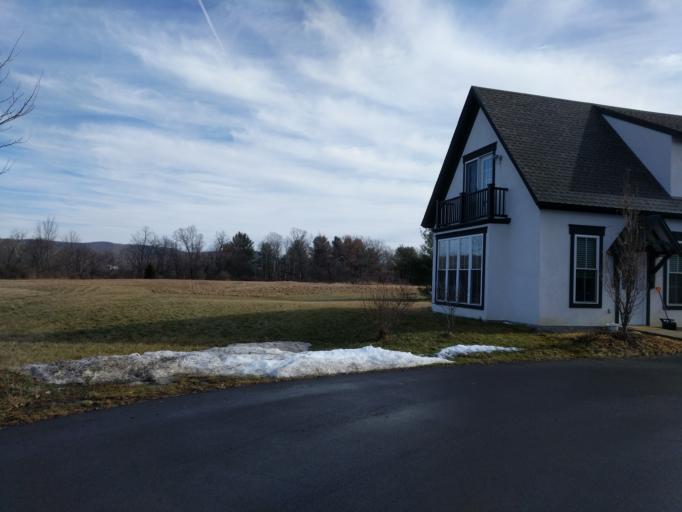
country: US
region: New York
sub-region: Tompkins County
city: Dryden
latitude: 42.3900
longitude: -76.3620
